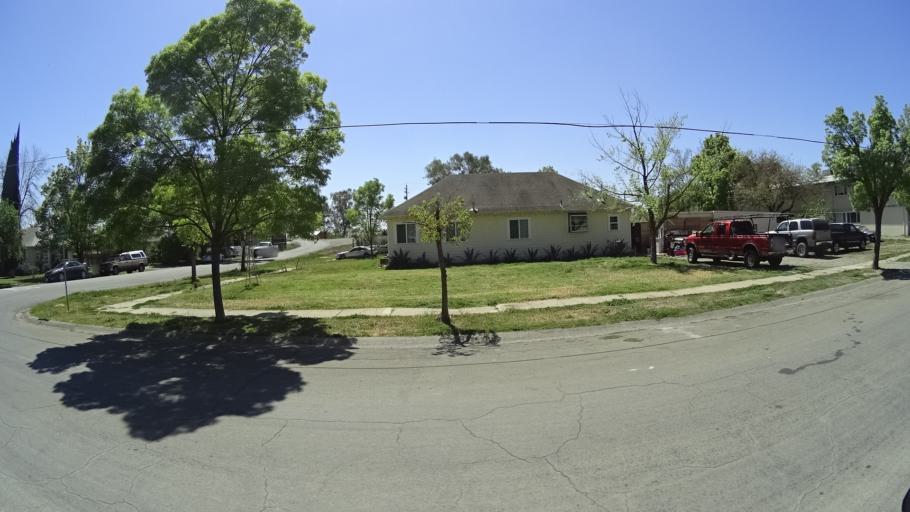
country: US
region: California
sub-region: Glenn County
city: Willows
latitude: 39.5180
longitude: -122.1897
